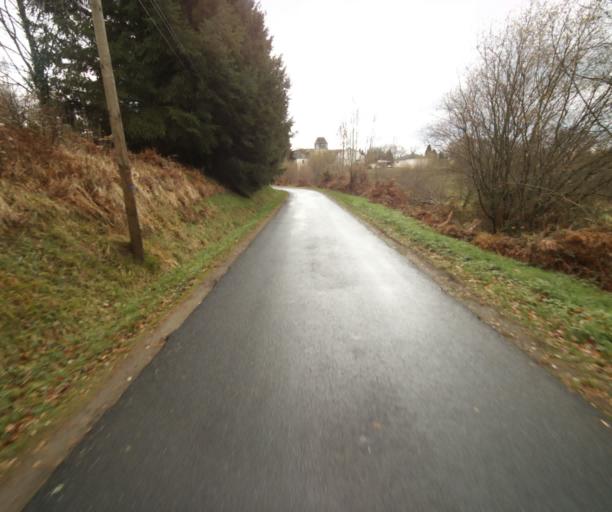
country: FR
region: Limousin
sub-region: Departement de la Correze
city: Saint-Mexant
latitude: 45.2767
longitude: 1.6355
